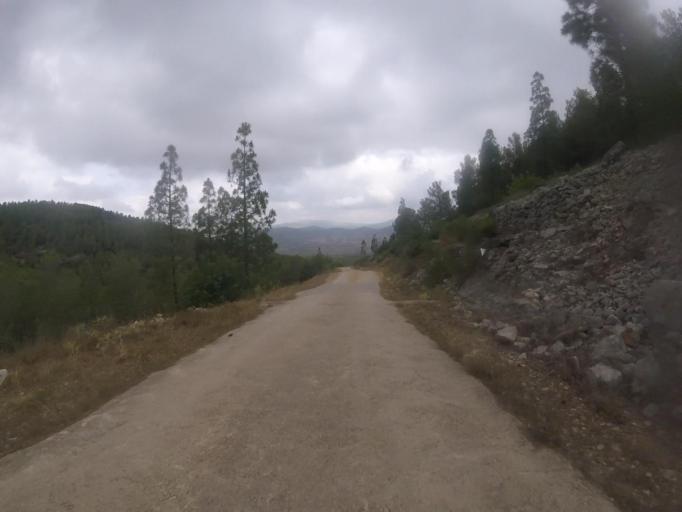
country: ES
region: Valencia
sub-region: Provincia de Castello
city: Santa Magdalena de Pulpis
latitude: 40.3307
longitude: 0.2807
